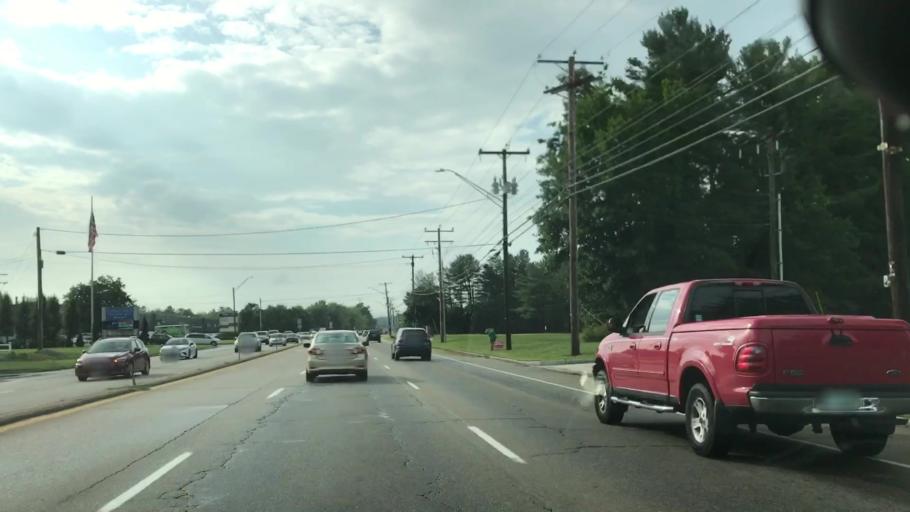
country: US
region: New Hampshire
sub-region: Hillsborough County
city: Nashua
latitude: 42.7942
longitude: -71.5252
